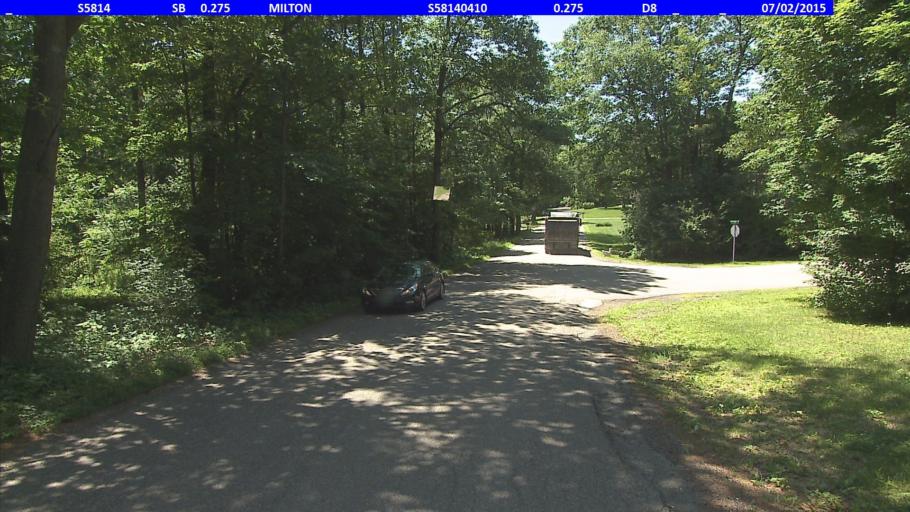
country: US
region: Vermont
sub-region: Chittenden County
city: Milton
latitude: 44.6341
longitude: -73.1763
